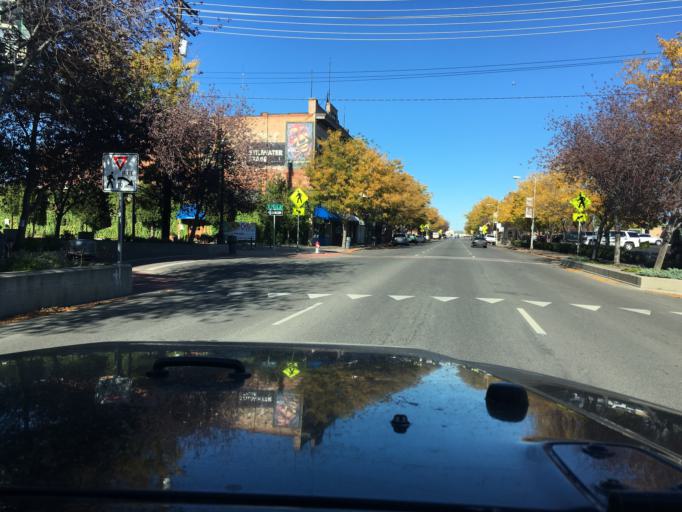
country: US
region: Montana
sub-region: Yellowstone County
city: Billings
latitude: 45.7829
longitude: -108.5015
